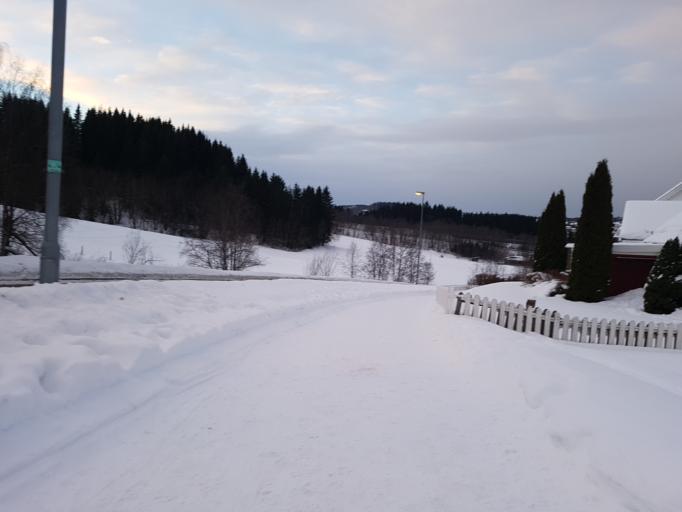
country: NO
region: Sor-Trondelag
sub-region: Trondheim
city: Trondheim
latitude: 63.3794
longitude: 10.3813
